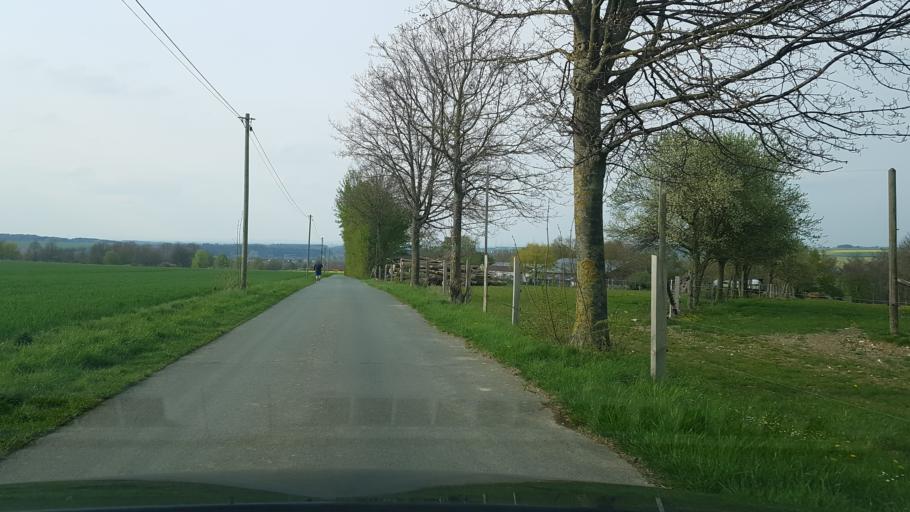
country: DE
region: North Rhine-Westphalia
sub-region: Regierungsbezirk Detmold
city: Paderborn
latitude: 51.6448
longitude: 8.7206
